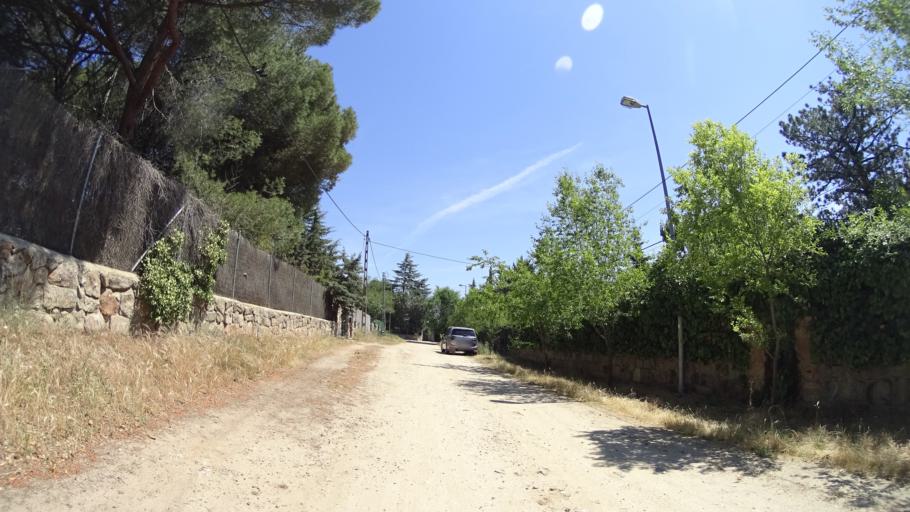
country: ES
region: Madrid
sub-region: Provincia de Madrid
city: Colmenarejo
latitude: 40.5540
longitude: -4.0053
